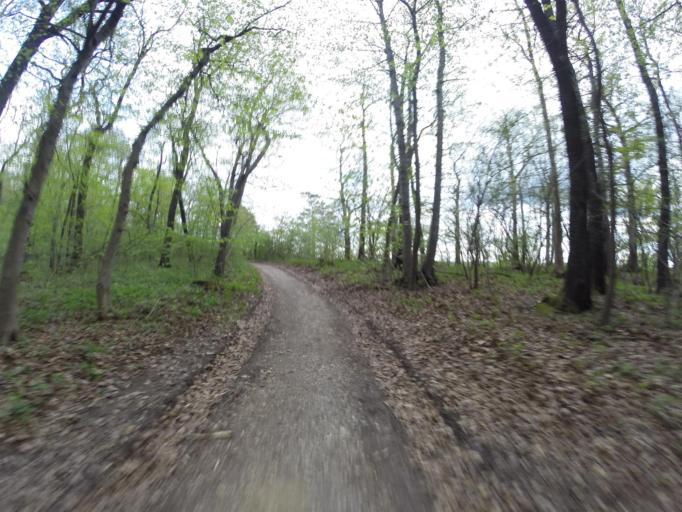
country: DE
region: Thuringia
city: Golmsdorf
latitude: 50.9546
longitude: 11.6622
